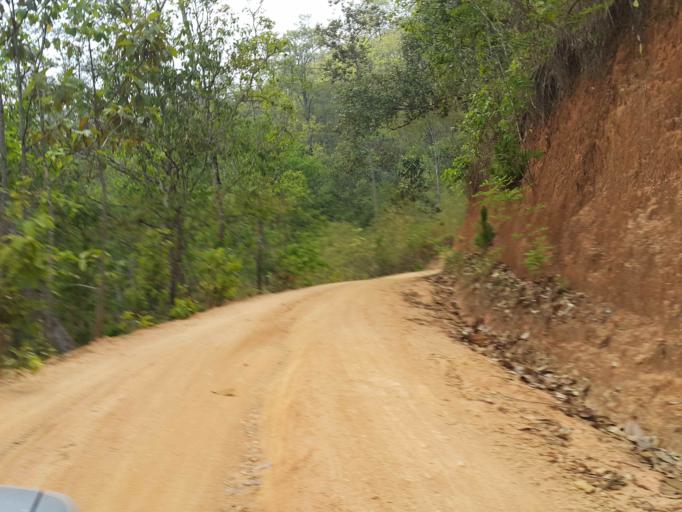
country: TH
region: Chiang Mai
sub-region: Amphoe Chiang Dao
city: Chiang Dao
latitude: 19.2892
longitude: 98.7571
